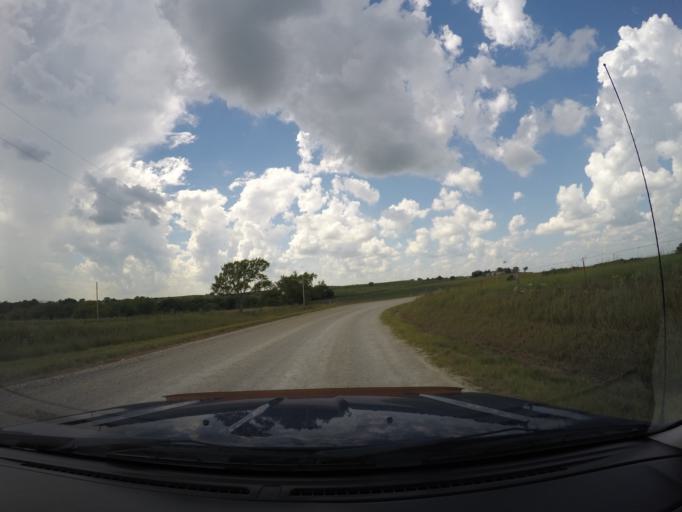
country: US
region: Kansas
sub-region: Wabaunsee County
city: Alma
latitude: 39.0256
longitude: -96.2974
